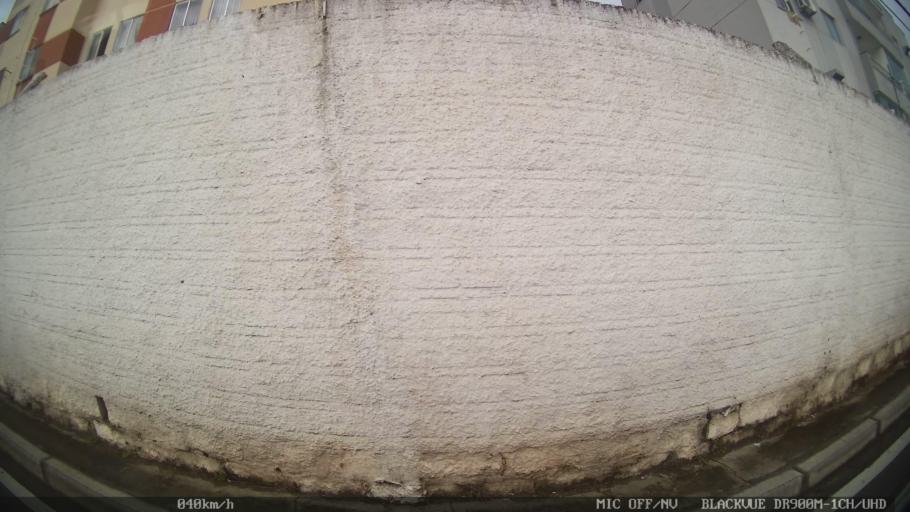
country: BR
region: Santa Catarina
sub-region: Sao Jose
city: Campinas
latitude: -27.5460
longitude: -48.6291
